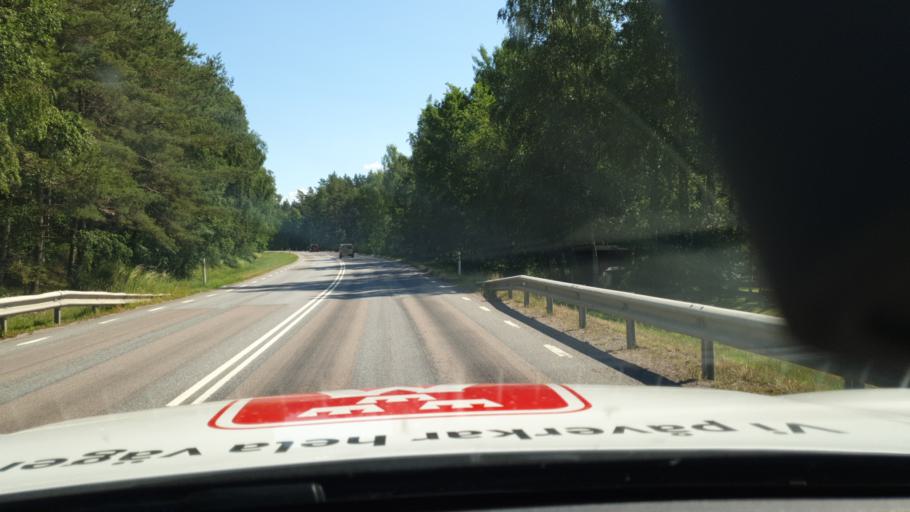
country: SE
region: Vaestra Goetaland
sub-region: Lidkopings Kommun
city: Lidkoping
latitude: 58.4980
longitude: 13.1303
